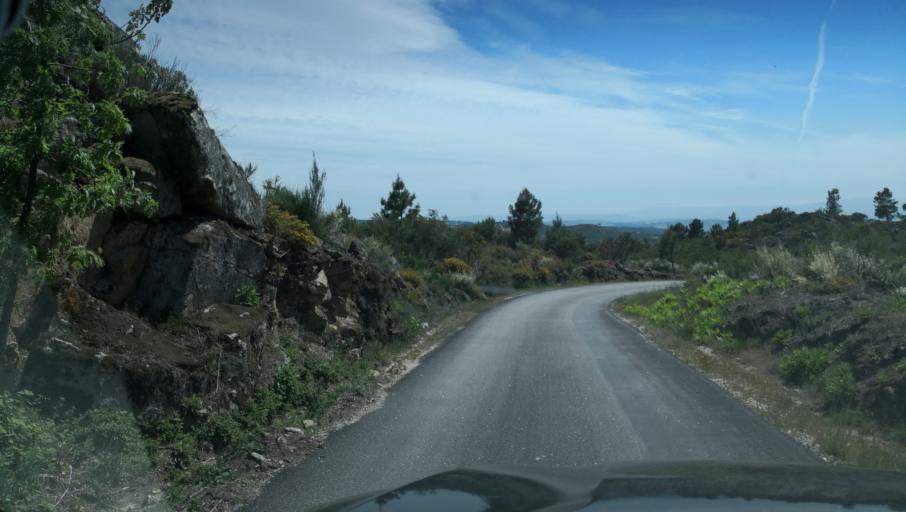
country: PT
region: Vila Real
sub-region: Vila Real
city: Vila Real
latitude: 41.3668
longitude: -7.6981
